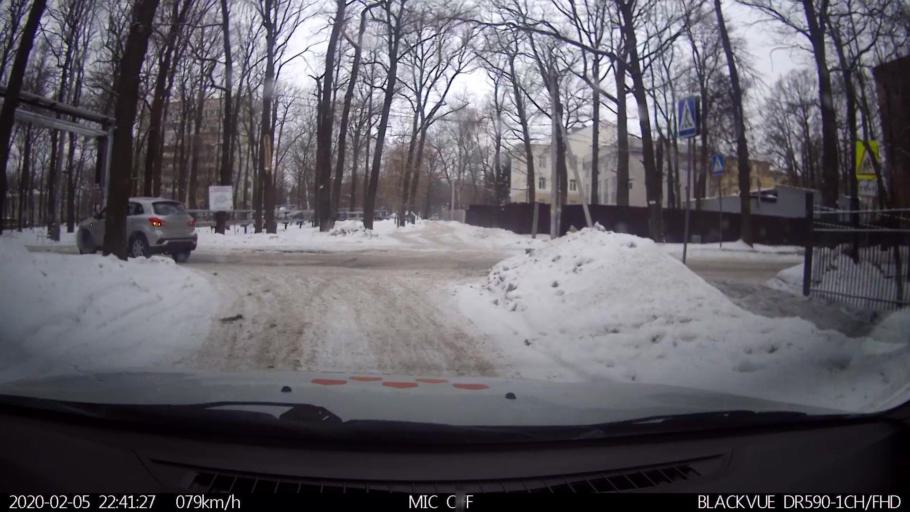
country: RU
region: Nizjnij Novgorod
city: Imeni Stepana Razina
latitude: 54.7206
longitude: 44.3384
